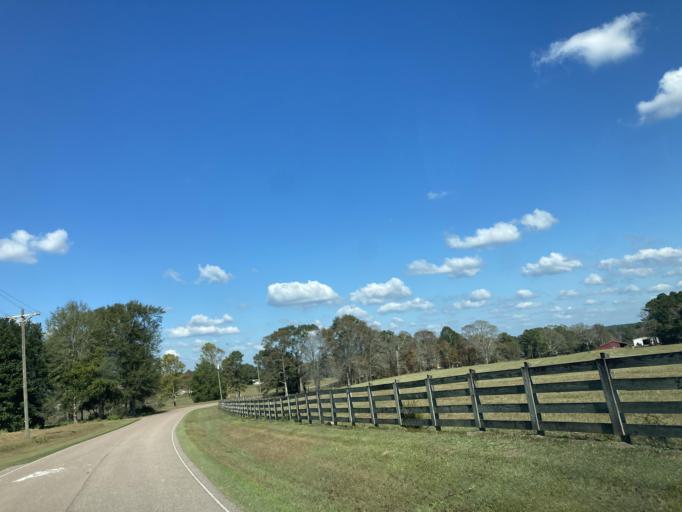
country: US
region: Mississippi
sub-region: Lamar County
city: Sumrall
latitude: 31.3007
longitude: -89.5410
